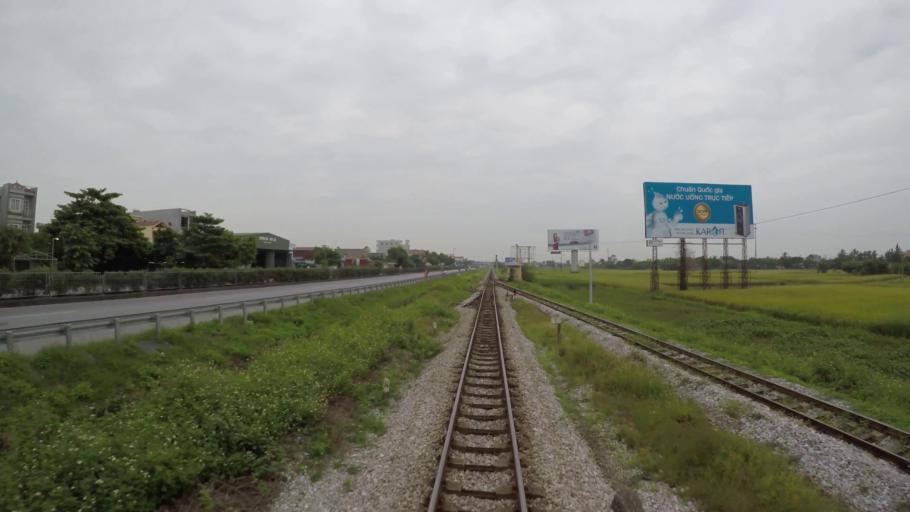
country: VN
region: Hai Duong
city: Phu Thai
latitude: 20.9309
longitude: 106.5536
